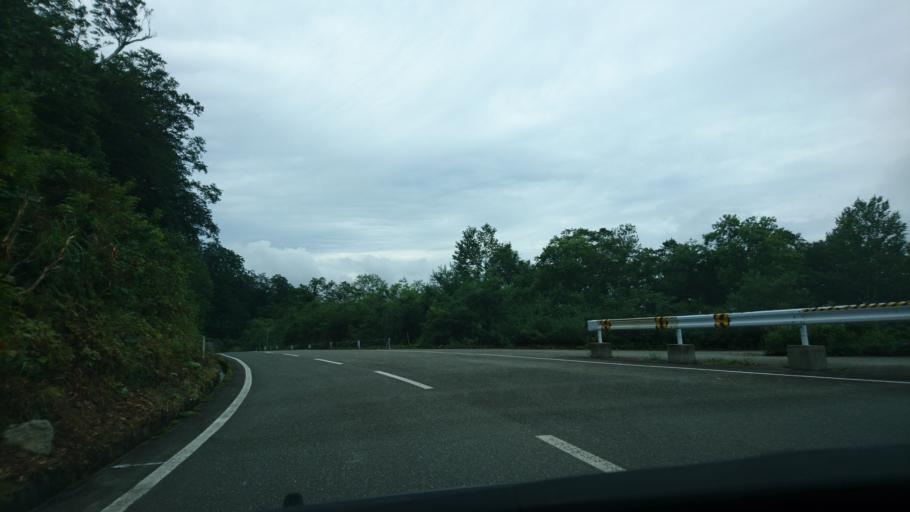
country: JP
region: Akita
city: Yuzawa
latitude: 38.9857
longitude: 140.7314
